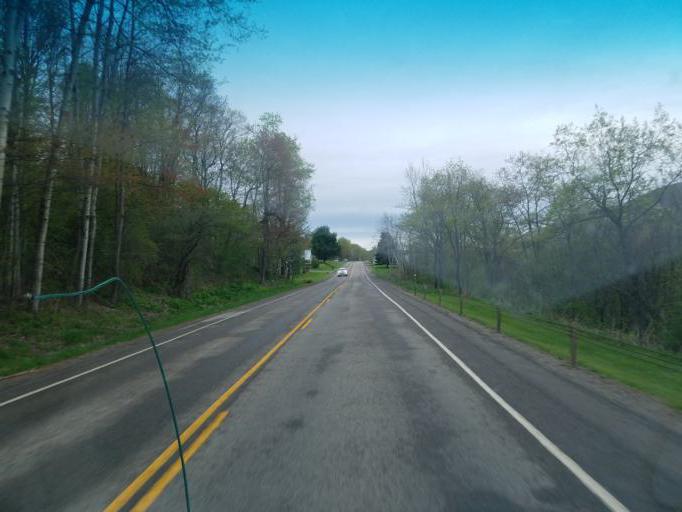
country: US
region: New York
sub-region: Allegany County
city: Wellsville
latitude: 42.0079
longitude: -77.8458
